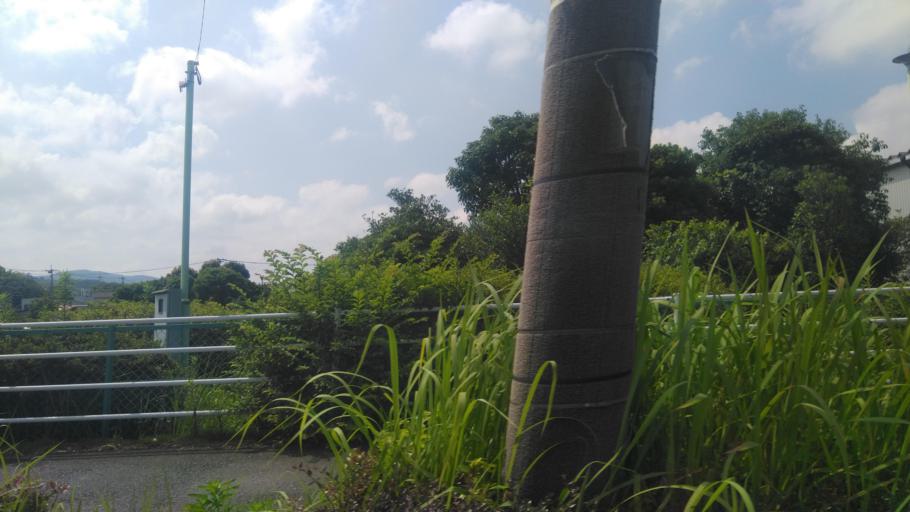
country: JP
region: Fukuoka
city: Onojo
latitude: 33.5671
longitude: 130.4650
